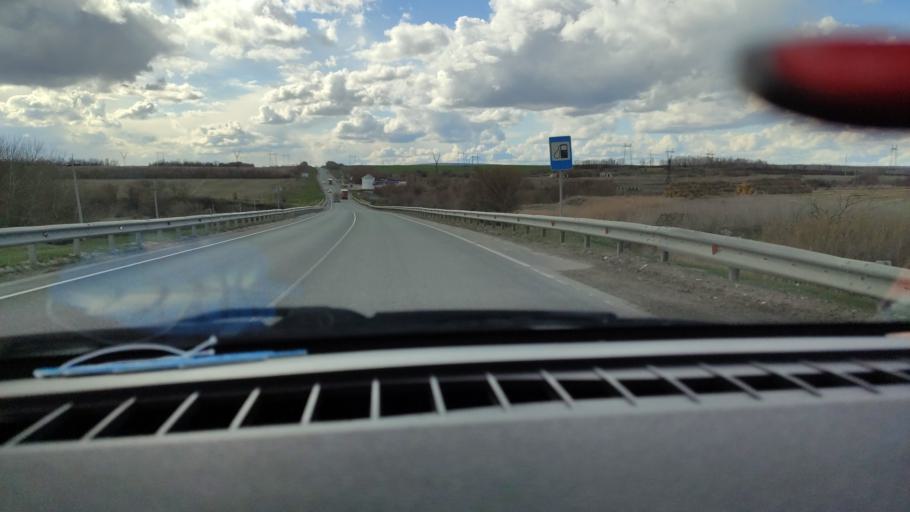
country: RU
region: Saratov
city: Tersa
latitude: 52.0986
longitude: 47.5260
